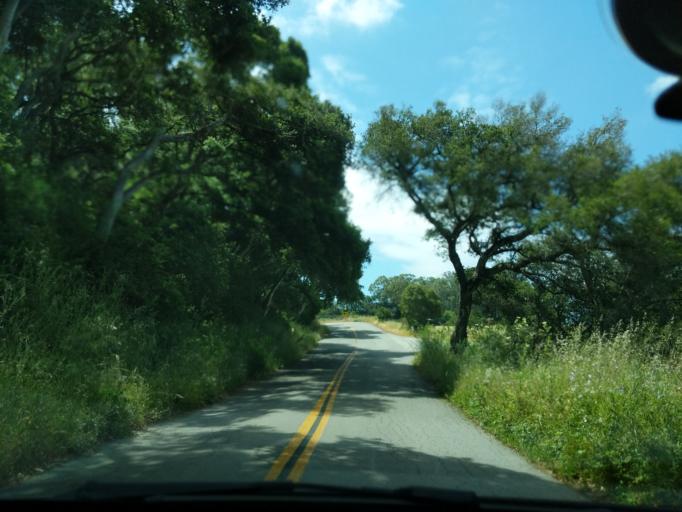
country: US
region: California
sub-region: Santa Cruz County
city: Freedom
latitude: 36.9286
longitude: -121.8016
